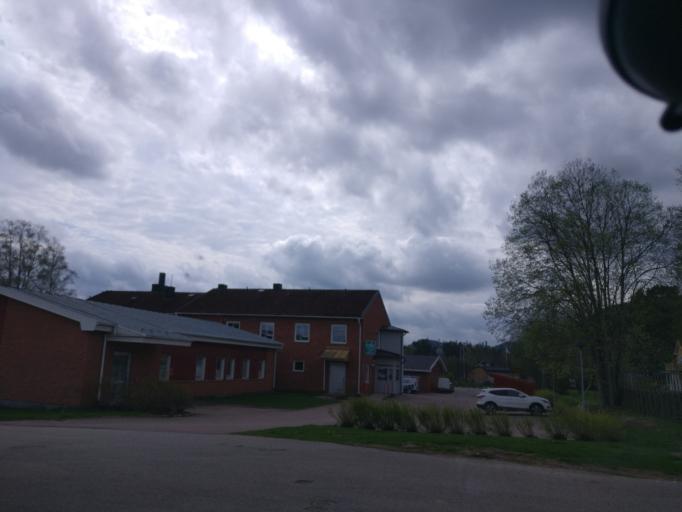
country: SE
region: Vaermland
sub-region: Hagfors Kommun
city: Ekshaerad
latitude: 60.1739
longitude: 13.4933
